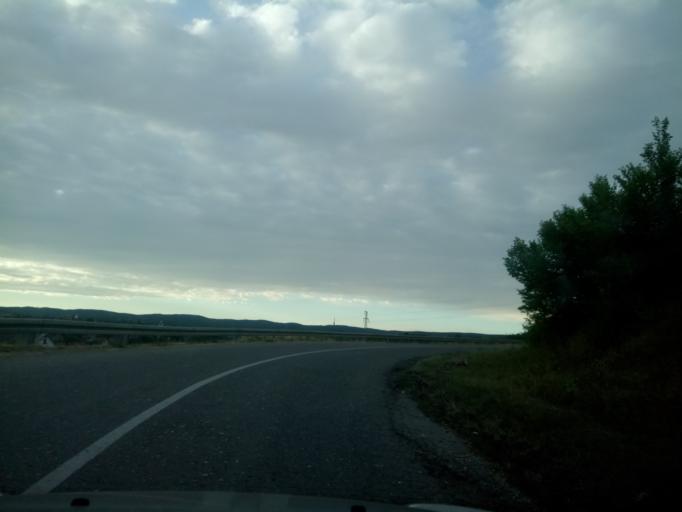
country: RS
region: Autonomna Pokrajina Vojvodina
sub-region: Sremski Okrug
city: Irig
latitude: 45.0930
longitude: 19.8664
